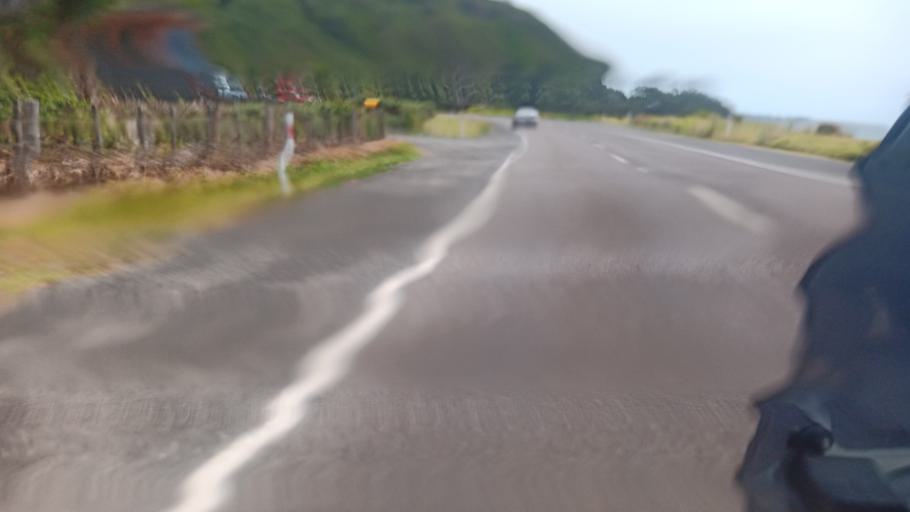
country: NZ
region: Bay of Plenty
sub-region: Opotiki District
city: Opotiki
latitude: -37.6190
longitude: 177.9422
